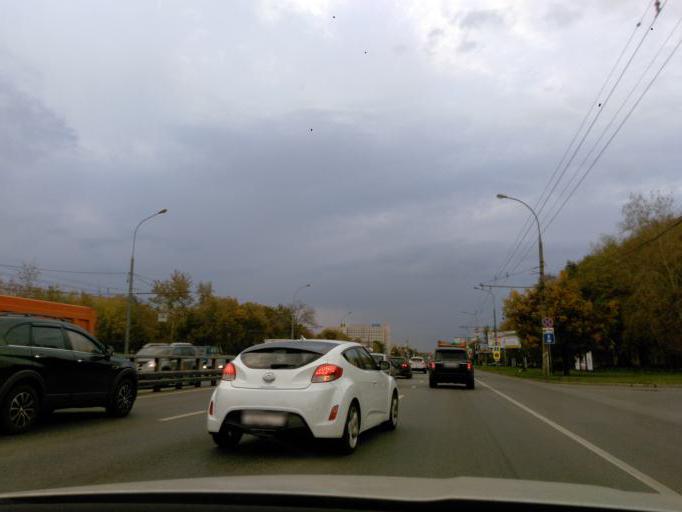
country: RU
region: Moscow
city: Novovladykino
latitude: 55.8152
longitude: 37.5765
